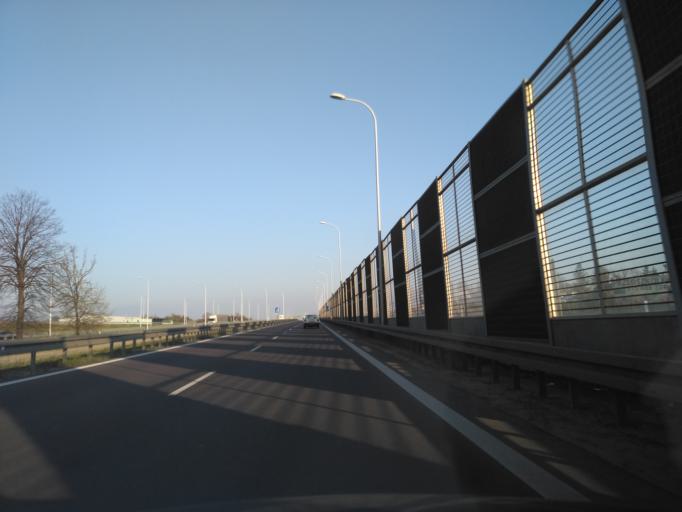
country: PL
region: Lublin Voivodeship
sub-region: Powiat swidnicki
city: Swidnik
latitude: 51.2071
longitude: 22.6577
